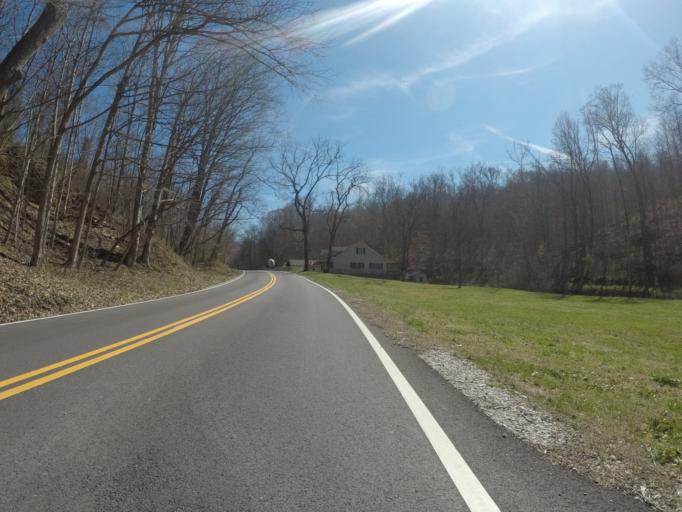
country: US
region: Ohio
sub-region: Lawrence County
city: South Point
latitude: 38.4625
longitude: -82.5592
